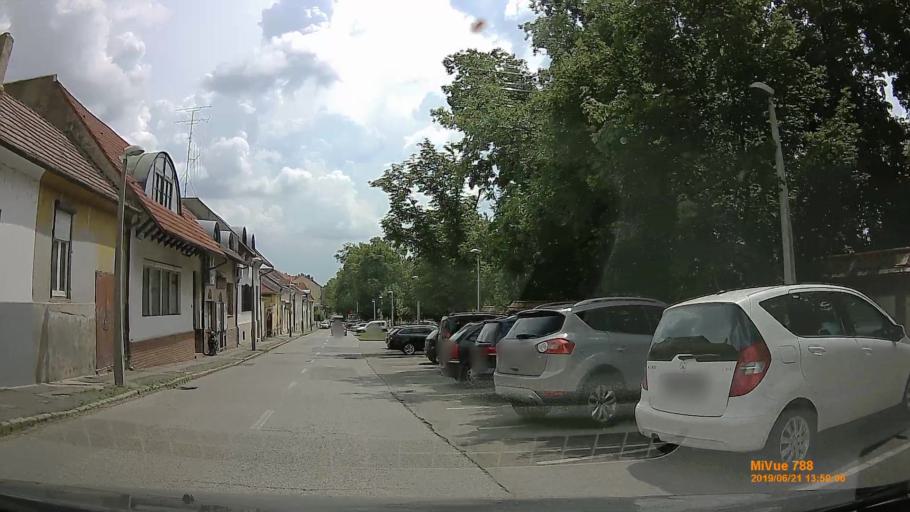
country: HU
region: Baranya
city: Pecs
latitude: 46.0727
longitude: 18.2228
